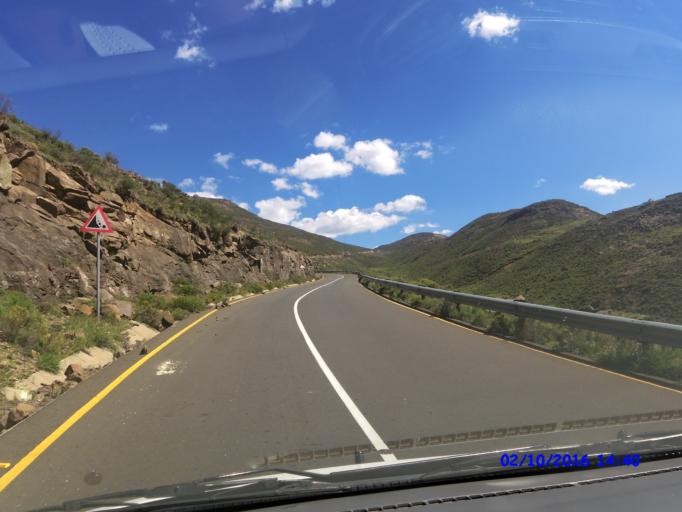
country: LS
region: Maseru
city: Nako
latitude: -29.5210
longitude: 28.0612
